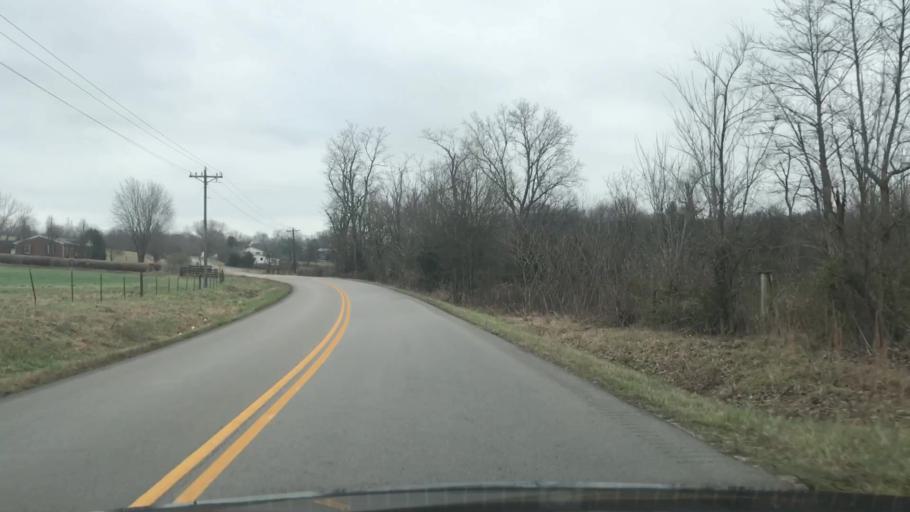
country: US
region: Kentucky
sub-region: Barren County
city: Glasgow
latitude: 36.9141
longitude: -85.8024
